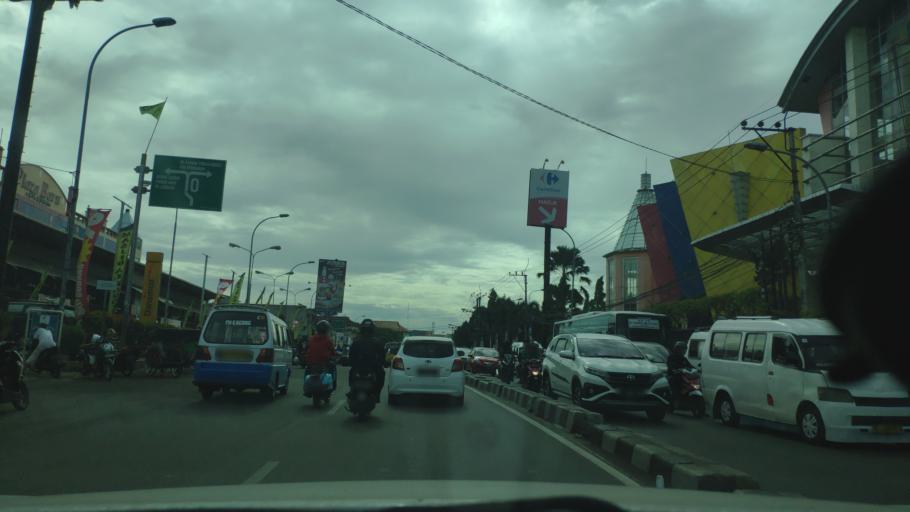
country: ID
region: West Java
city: Ciputat
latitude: -6.2248
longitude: 106.7087
